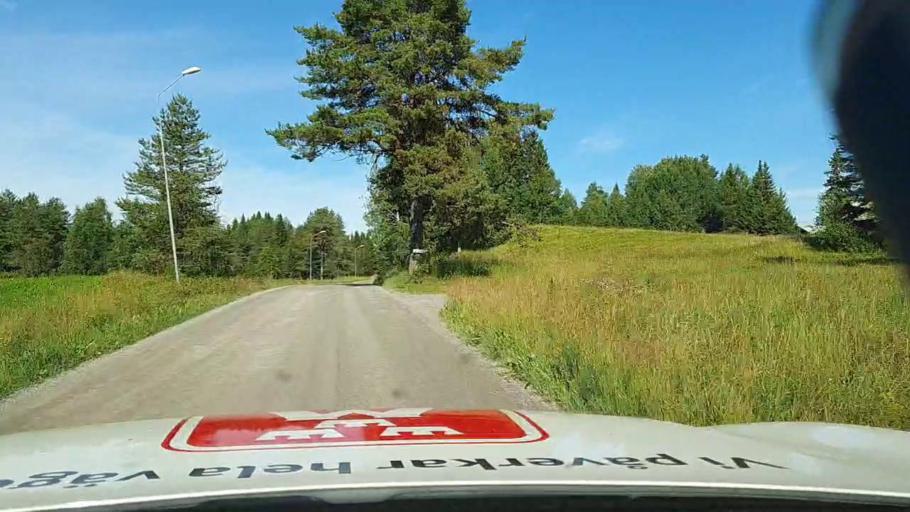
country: SE
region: Jaemtland
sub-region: Stroemsunds Kommun
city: Stroemsund
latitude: 63.6810
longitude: 15.3886
